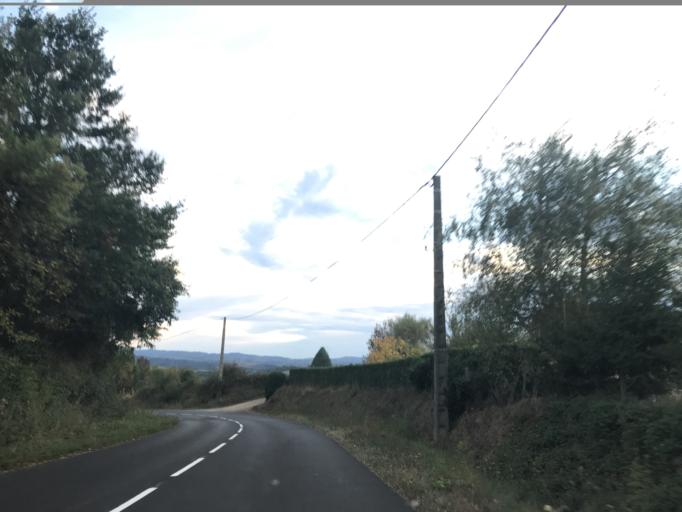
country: FR
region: Auvergne
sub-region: Departement du Puy-de-Dome
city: Escoutoux
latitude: 45.7811
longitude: 3.5984
